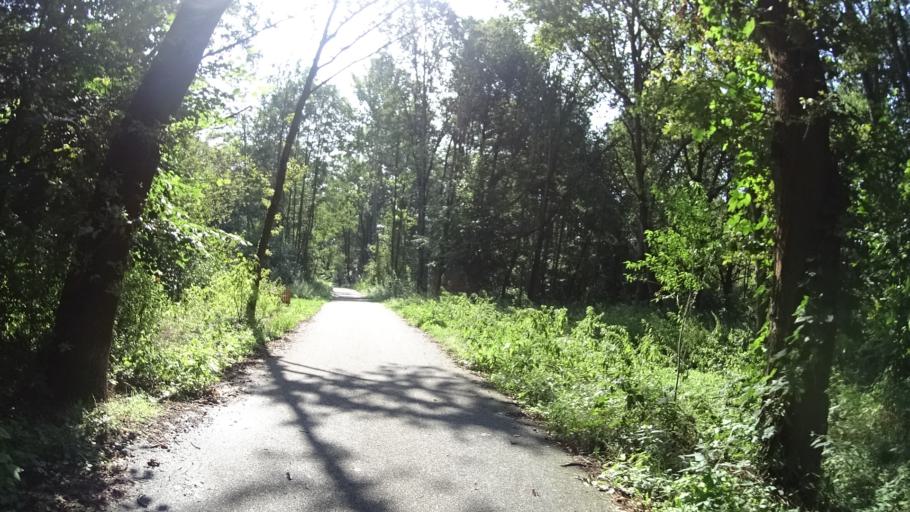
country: DE
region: Brandenburg
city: Burg
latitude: 51.8260
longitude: 14.1498
